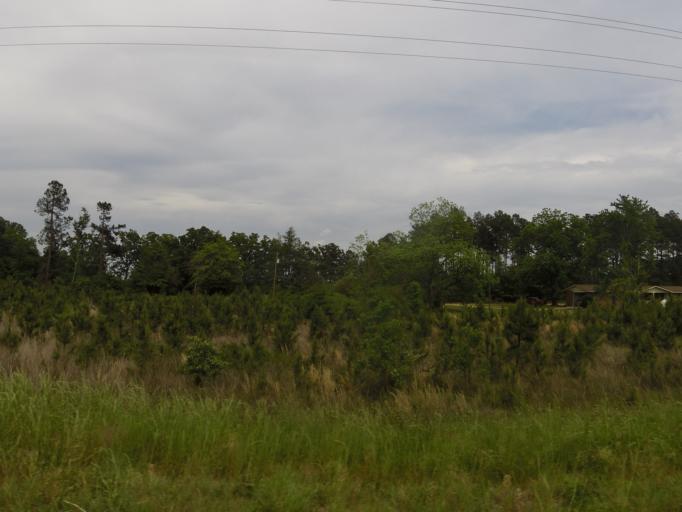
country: US
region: Georgia
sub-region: Jefferson County
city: Wrens
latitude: 33.3142
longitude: -82.4477
